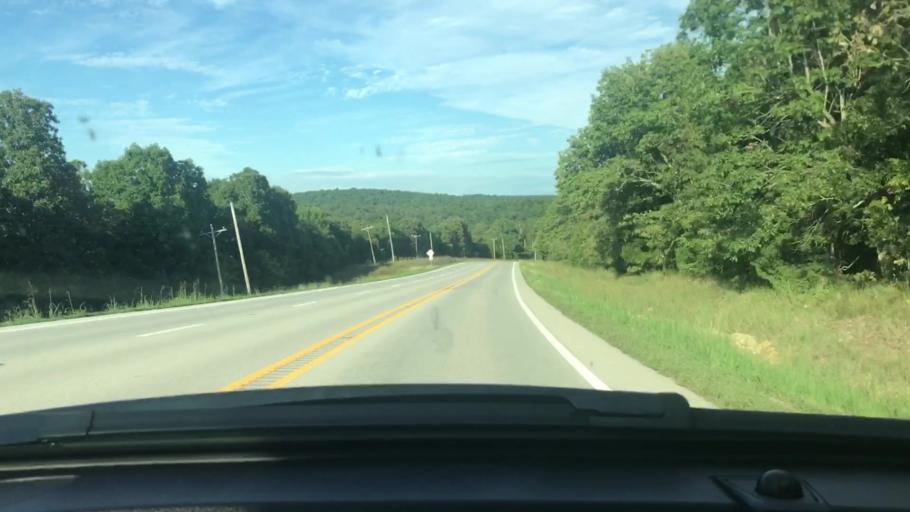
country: US
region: Arkansas
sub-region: Sharp County
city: Cherokee Village
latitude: 36.2737
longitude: -91.3647
